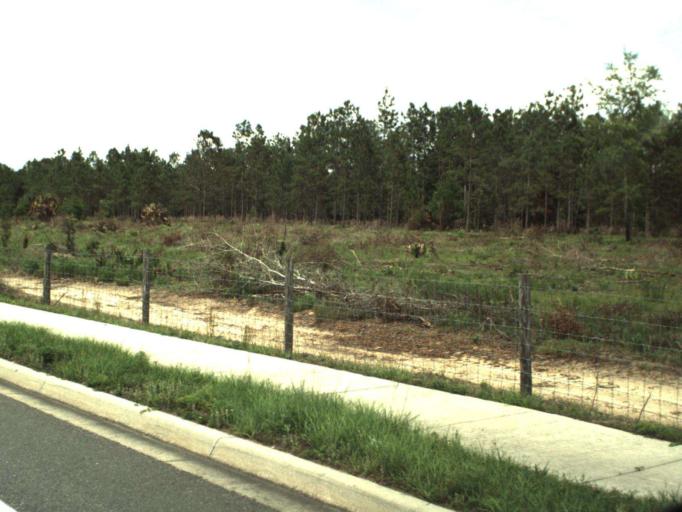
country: US
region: Florida
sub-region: Marion County
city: Ocala
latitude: 29.1954
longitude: -82.0535
